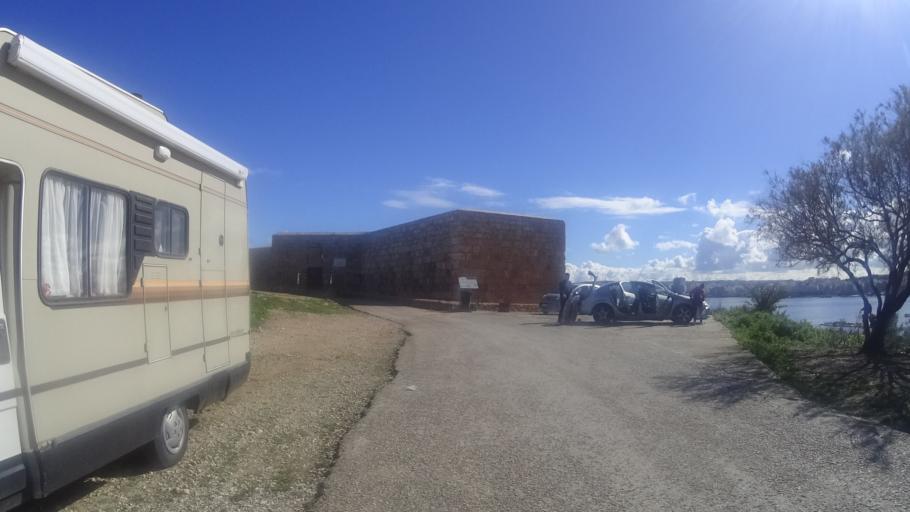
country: MT
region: Saint Paul's Bay
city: San Pawl il-Bahar
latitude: 35.9586
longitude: 14.3944
